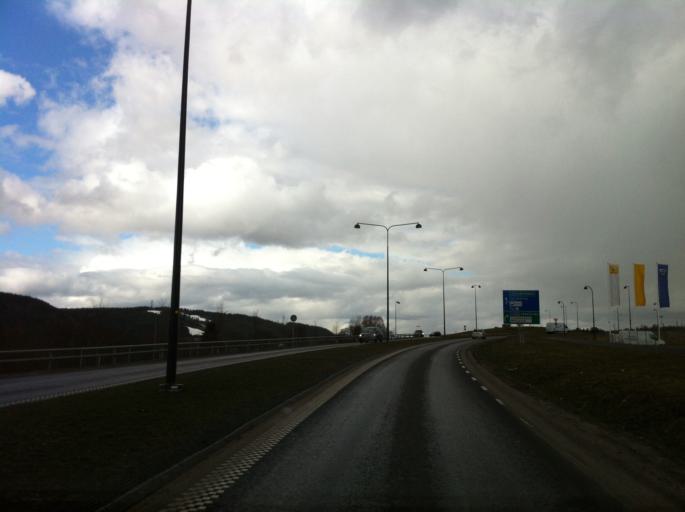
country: SE
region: Vaestra Goetaland
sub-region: Ulricehamns Kommun
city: Ulricehamn
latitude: 57.7401
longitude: 13.4333
